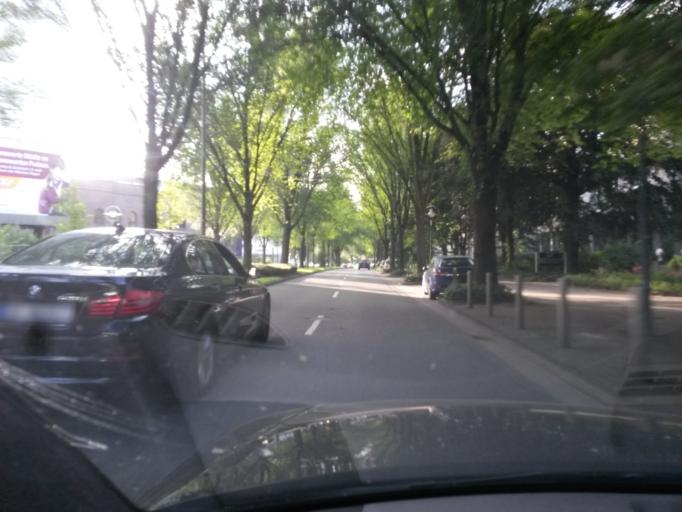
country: DE
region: North Rhine-Westphalia
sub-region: Regierungsbezirk Arnsberg
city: Dortmund
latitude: 51.5032
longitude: 7.4789
